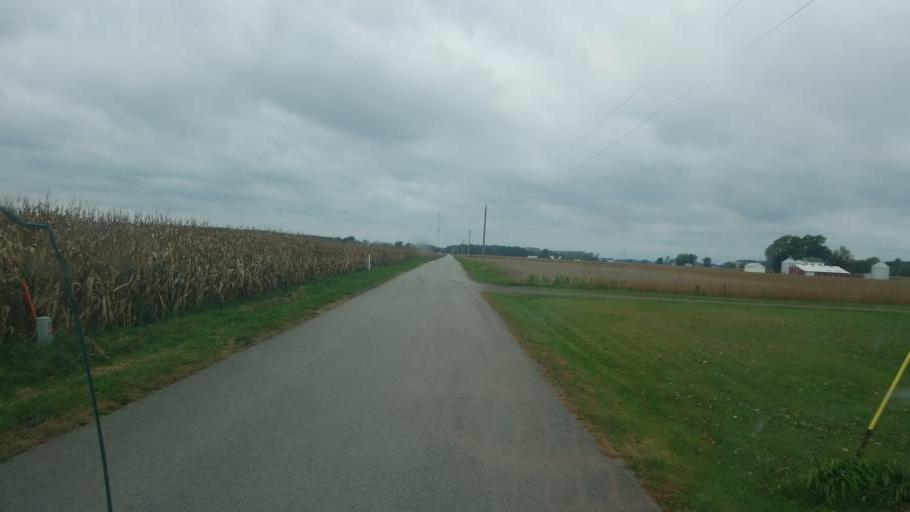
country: US
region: Ohio
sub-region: Seneca County
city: Fostoria
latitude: 41.0792
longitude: -83.5001
